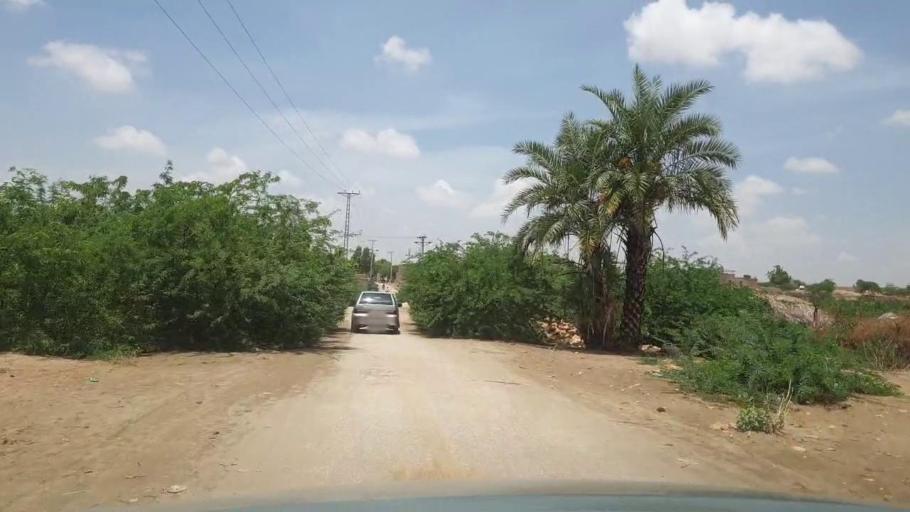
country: PK
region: Sindh
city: Kot Diji
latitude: 27.1593
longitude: 68.9669
